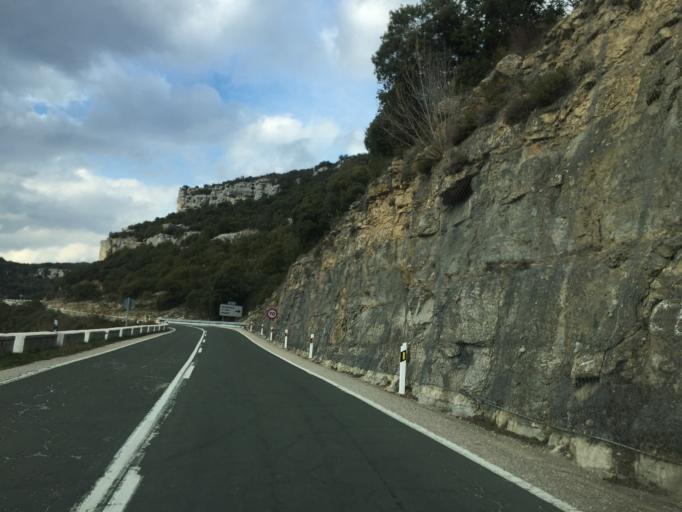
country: ES
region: Cantabria
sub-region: Provincia de Cantabria
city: San Martin de Elines
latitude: 42.8126
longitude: -3.7714
